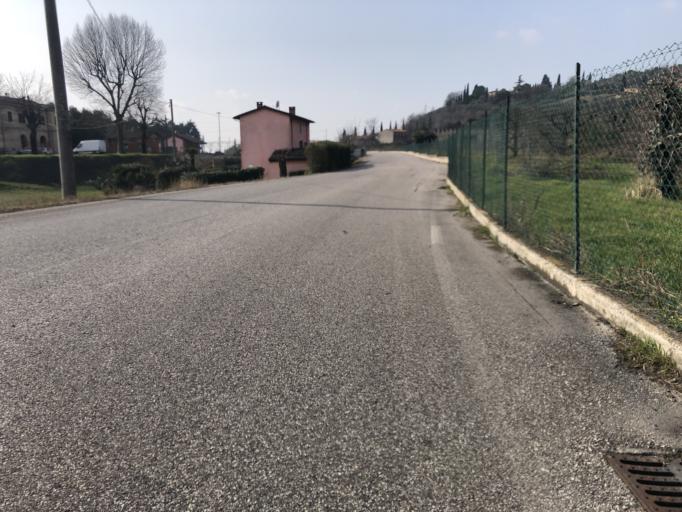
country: IT
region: Veneto
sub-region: Provincia di Verona
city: Sona
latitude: 45.4274
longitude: 10.8452
